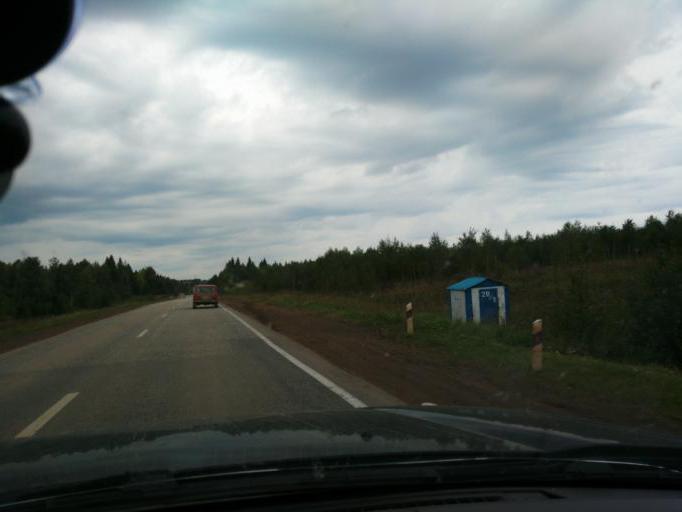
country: RU
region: Perm
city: Chernushka
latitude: 56.8045
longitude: 56.0632
